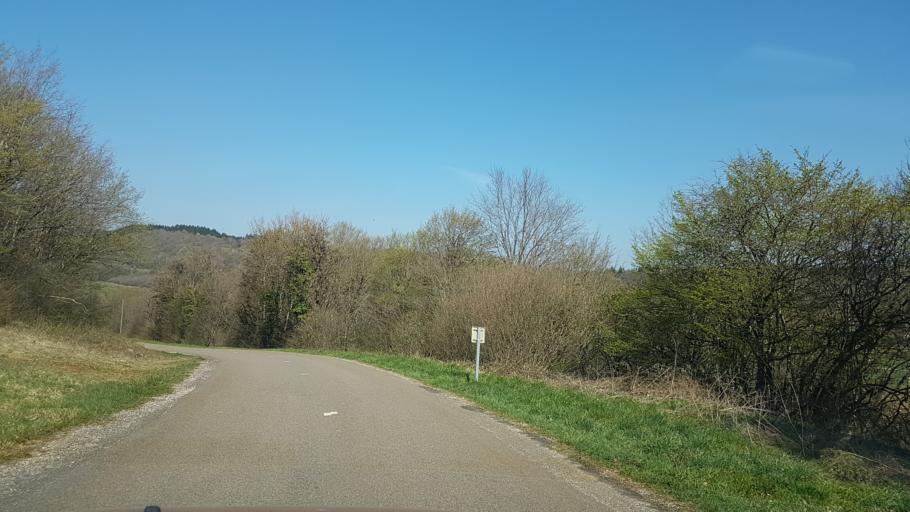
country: FR
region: Franche-Comte
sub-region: Departement du Jura
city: Orgelet
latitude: 46.5044
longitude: 5.5278
